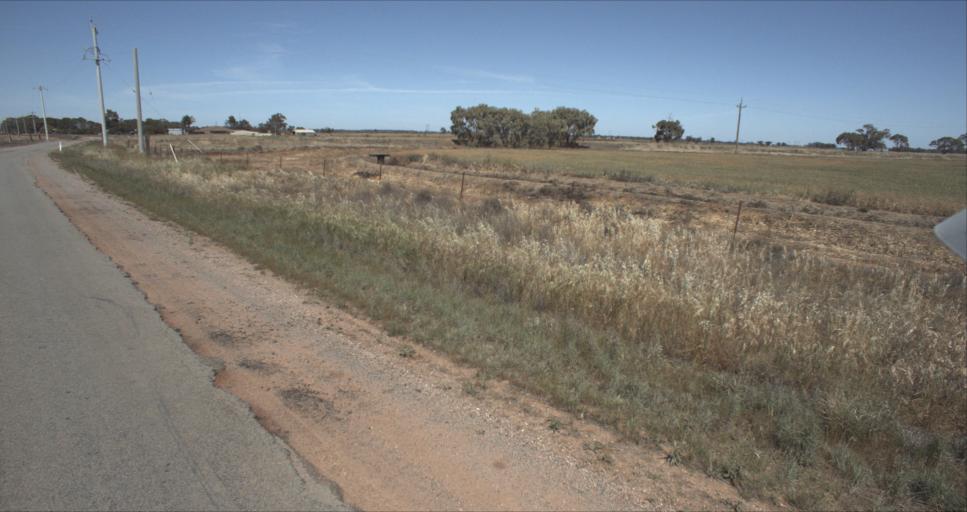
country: AU
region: New South Wales
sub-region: Leeton
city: Leeton
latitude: -34.5663
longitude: 146.3117
